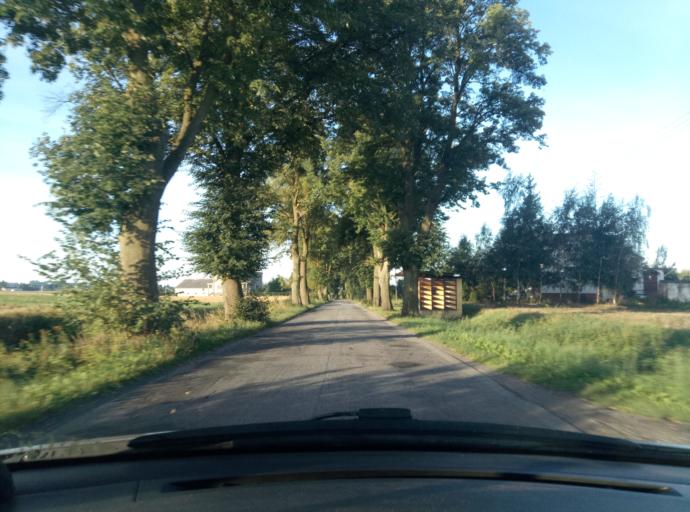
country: PL
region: Kujawsko-Pomorskie
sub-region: Powiat brodnicki
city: Jablonowo Pomorskie
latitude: 53.4047
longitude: 19.1705
